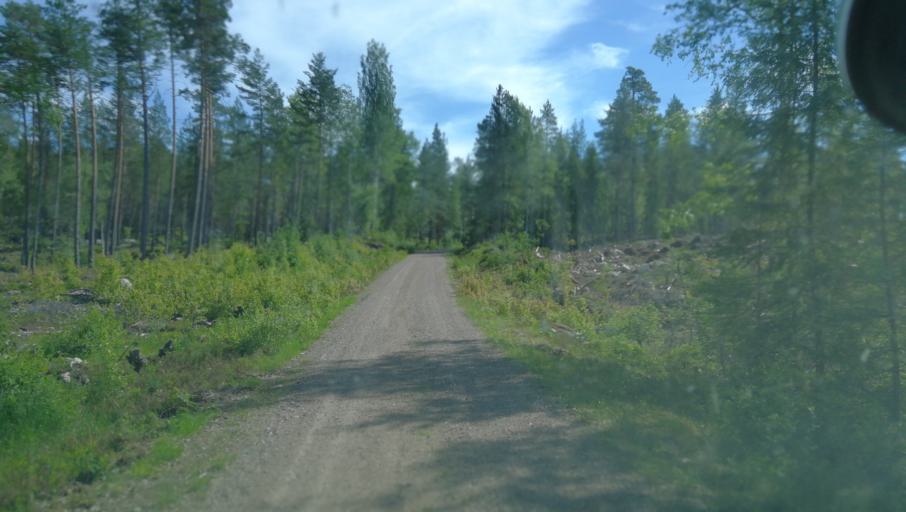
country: SE
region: Dalarna
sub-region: Vansbro Kommun
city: Vansbro
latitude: 60.8338
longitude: 14.1615
